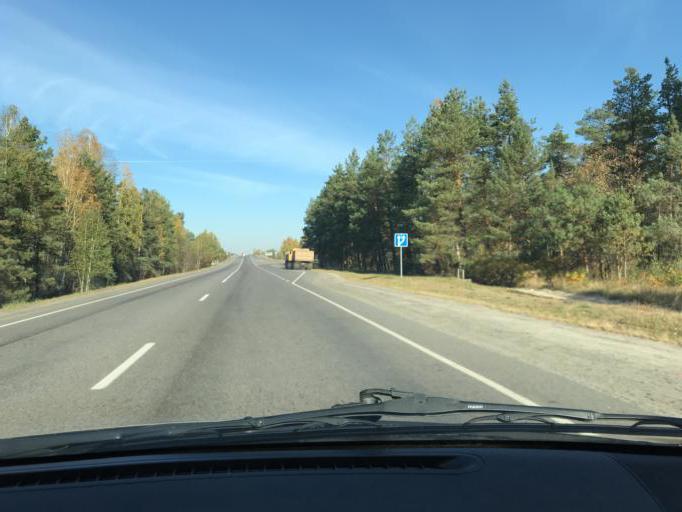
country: BY
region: Brest
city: Mikashevichy
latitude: 52.2391
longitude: 27.4471
